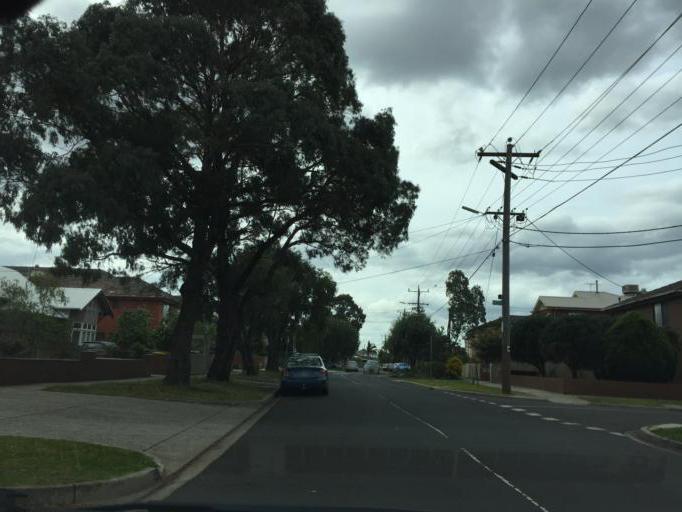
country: AU
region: Victoria
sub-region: Maribyrnong
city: Kingsville
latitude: -37.8087
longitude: 144.8787
